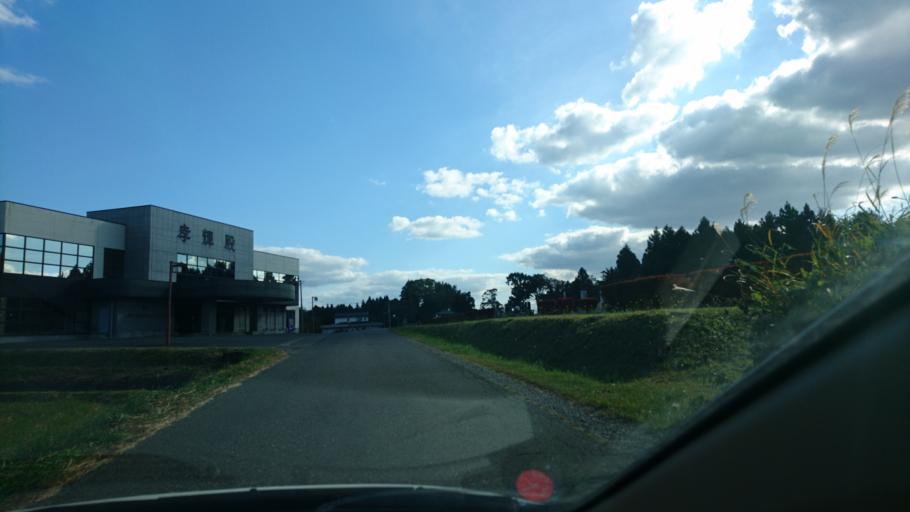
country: JP
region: Iwate
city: Kitakami
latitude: 39.2503
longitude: 141.1242
